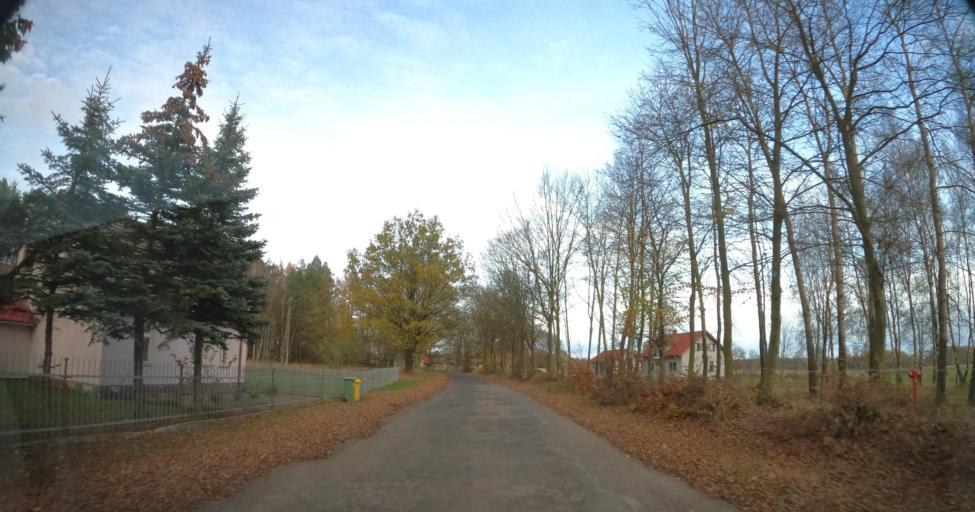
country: PL
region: West Pomeranian Voivodeship
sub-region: Powiat goleniowski
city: Osina
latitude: 53.6970
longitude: 14.9597
